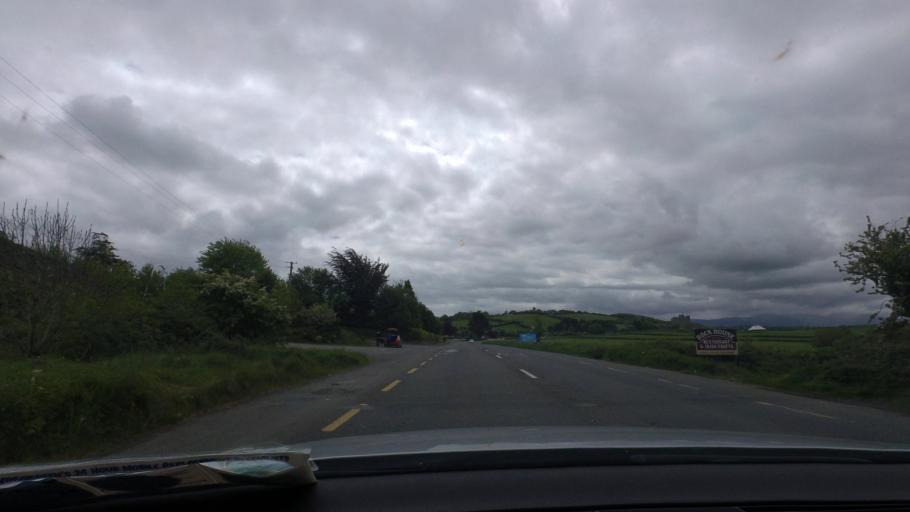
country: IE
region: Munster
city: Cashel
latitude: 52.5322
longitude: -7.8780
